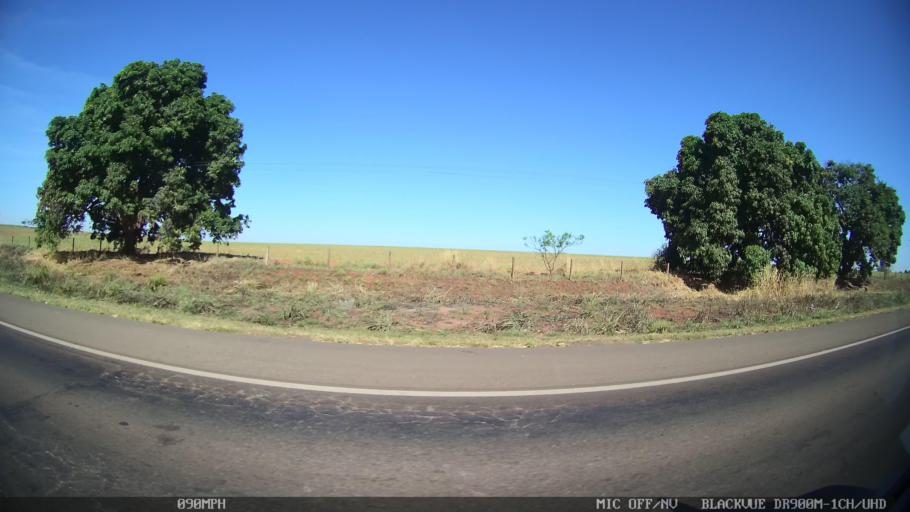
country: BR
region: Sao Paulo
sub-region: Olimpia
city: Olimpia
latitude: -20.6800
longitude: -48.8942
